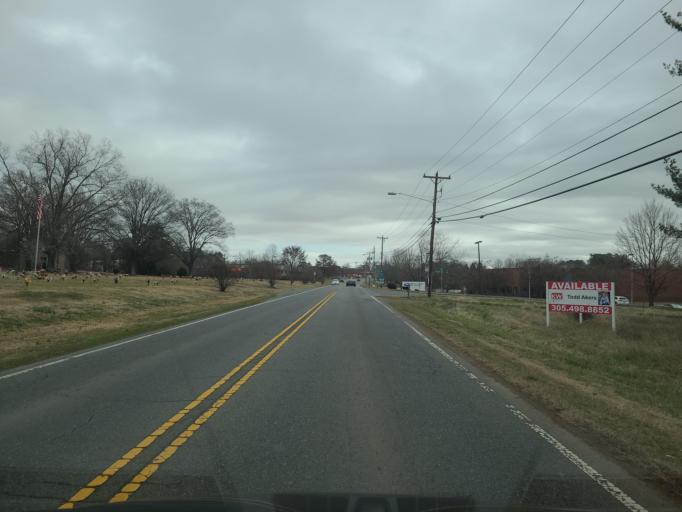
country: US
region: North Carolina
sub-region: Mecklenburg County
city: Mint Hill
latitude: 35.1887
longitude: -80.6939
